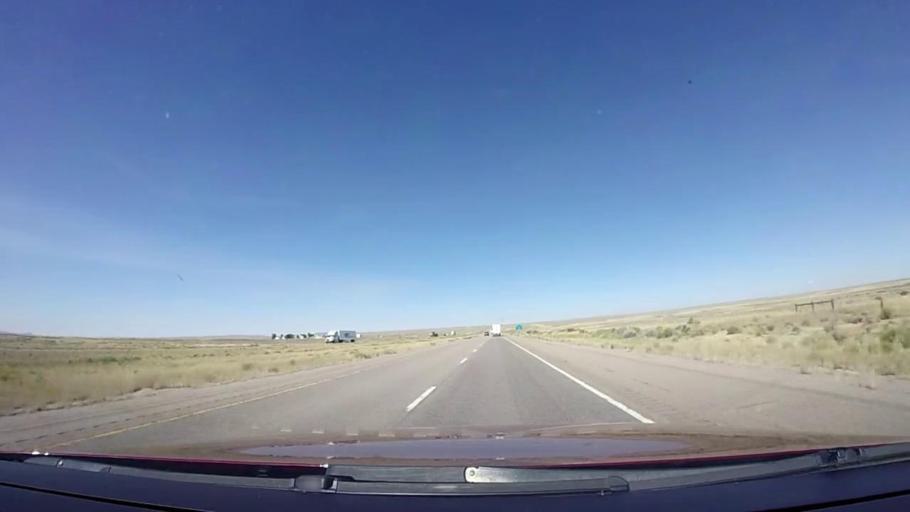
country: US
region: Wyoming
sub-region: Sweetwater County
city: Rock Springs
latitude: 41.6399
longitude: -108.4805
